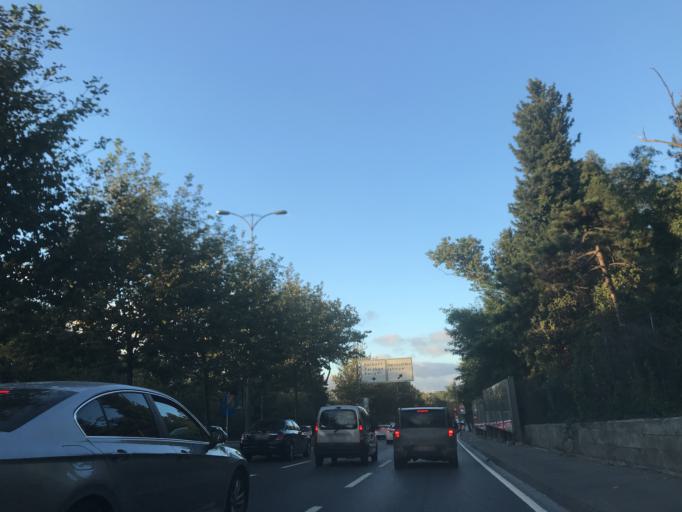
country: TR
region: Istanbul
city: Sisli
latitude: 41.1248
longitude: 29.0238
